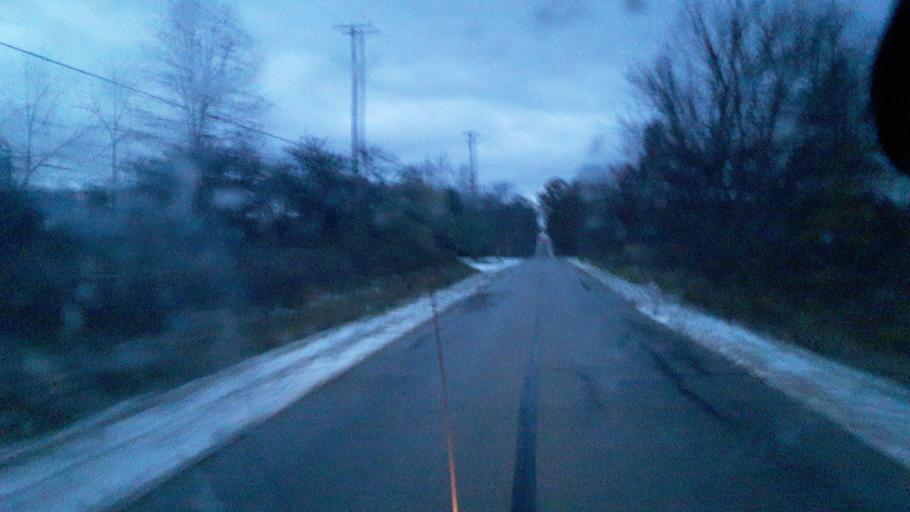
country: US
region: Ohio
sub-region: Portage County
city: Hiram
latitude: 41.3658
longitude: -81.1531
